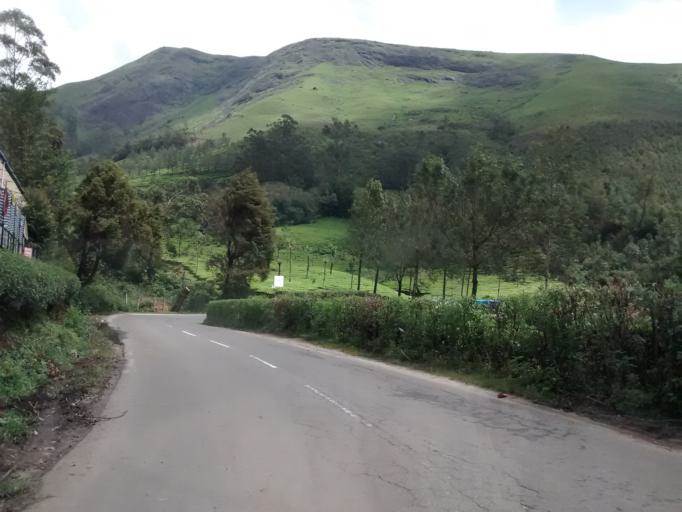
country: IN
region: Kerala
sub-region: Idukki
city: Munnar
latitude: 10.0962
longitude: 77.1017
